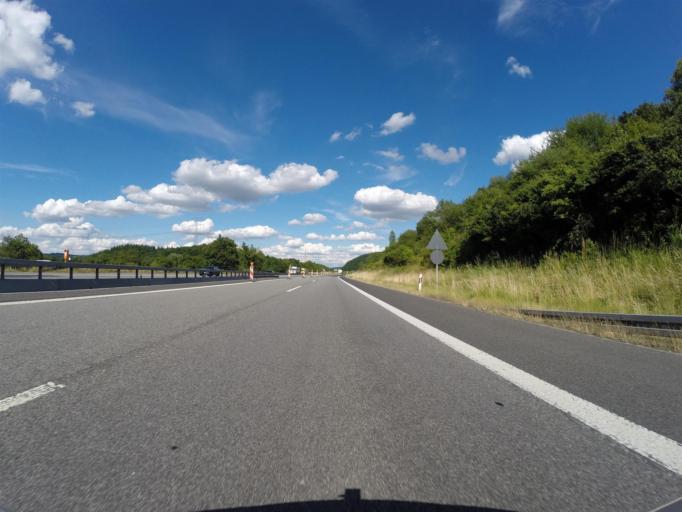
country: DE
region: Bavaria
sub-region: Regierungsbezirk Unterfranken
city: Sand
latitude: 49.9771
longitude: 10.6154
